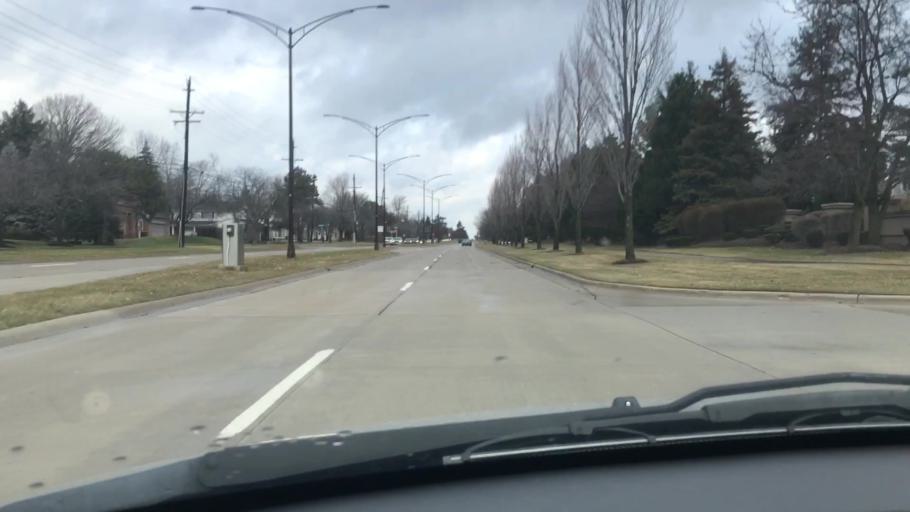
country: US
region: Michigan
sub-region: Oakland County
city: Birmingham
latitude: 42.5670
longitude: -83.1871
